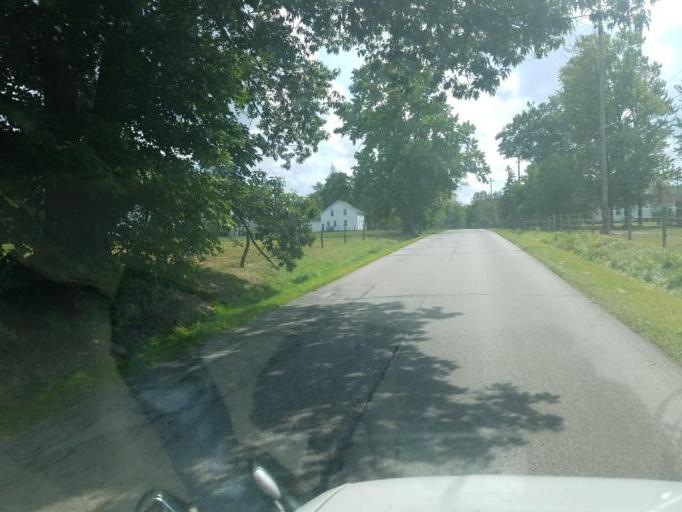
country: US
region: Ohio
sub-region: Geauga County
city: Middlefield
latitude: 41.4539
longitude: -81.1087
